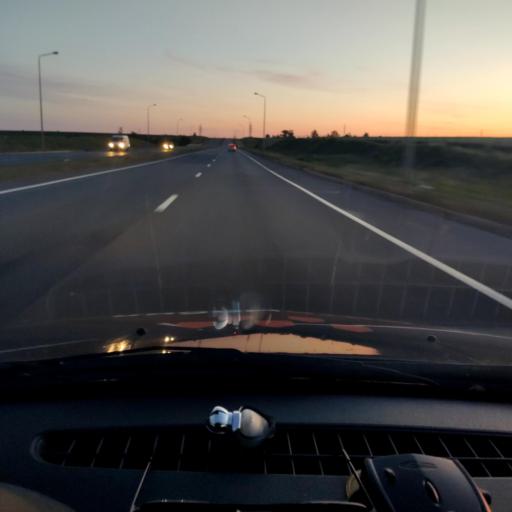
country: RU
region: Belgorod
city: Staryy Oskol
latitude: 51.3246
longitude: 37.7236
